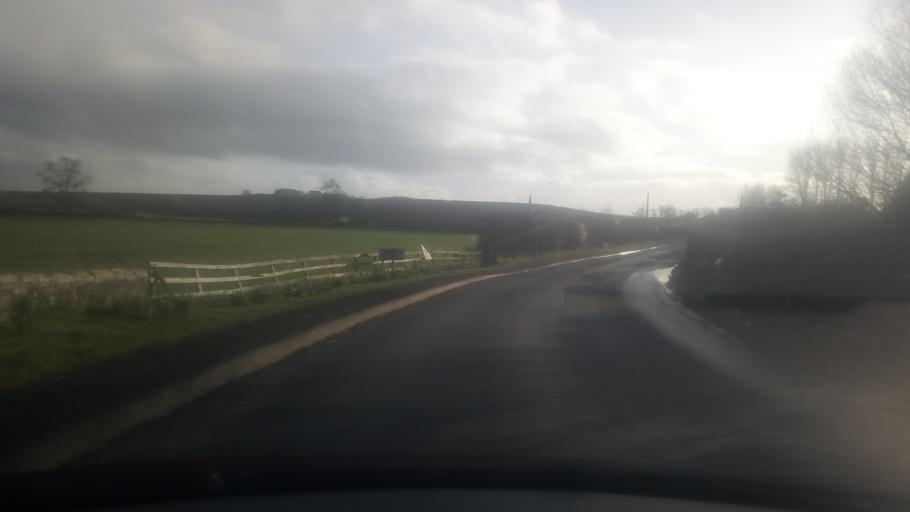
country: GB
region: Scotland
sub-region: The Scottish Borders
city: Kelso
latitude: 55.6274
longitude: -2.4160
